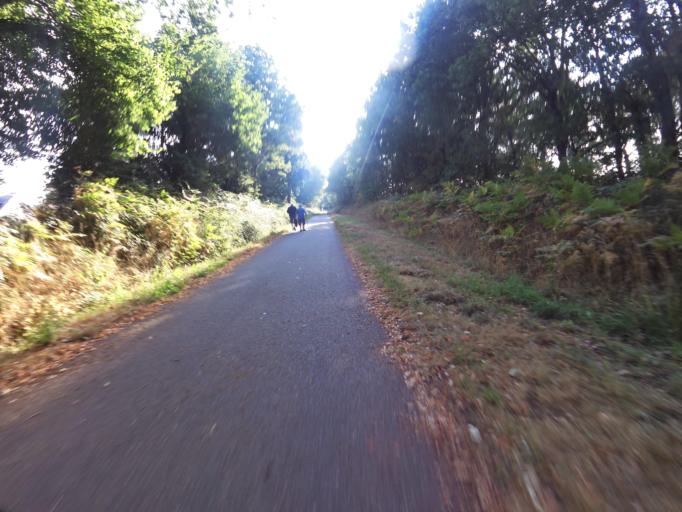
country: FR
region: Brittany
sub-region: Departement du Morbihan
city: Ploermel
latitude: 47.9232
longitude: -2.4180
